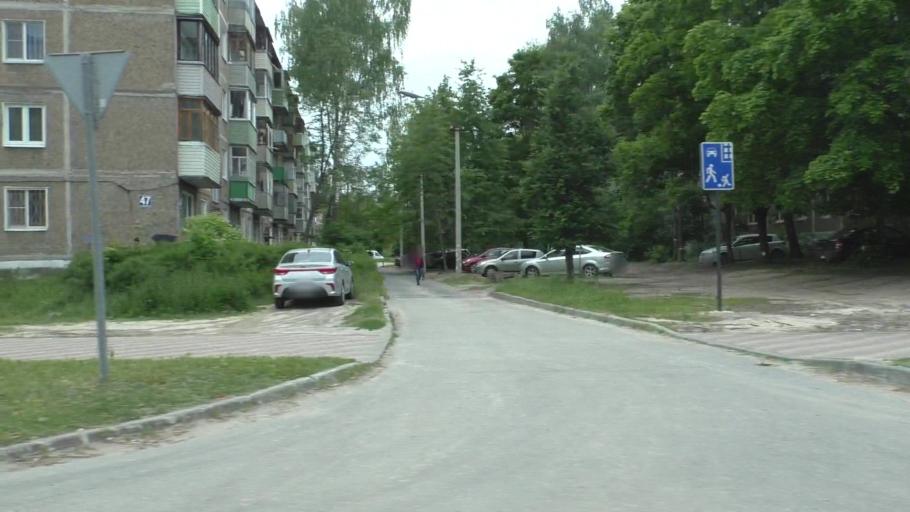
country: RU
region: Moskovskaya
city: Yegor'yevsk
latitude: 55.3656
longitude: 39.0631
